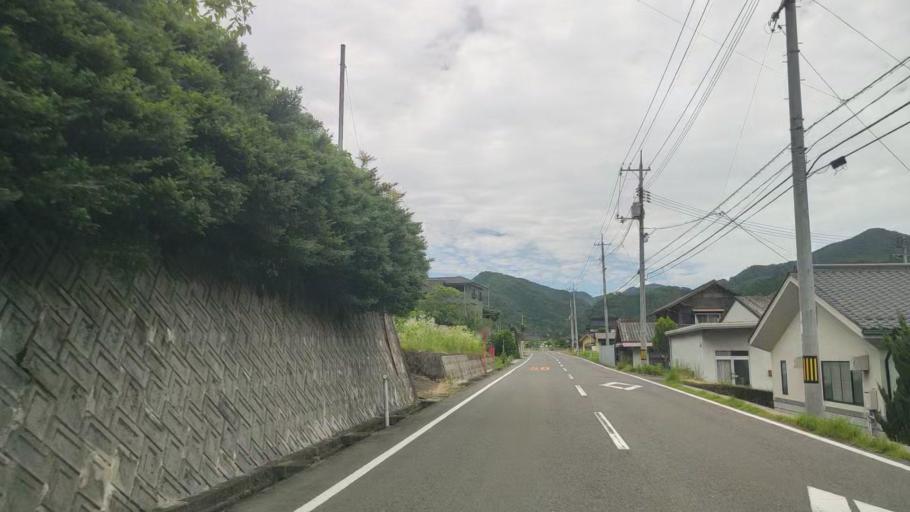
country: JP
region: Hyogo
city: Yamazakicho-nakabirose
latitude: 35.0959
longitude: 134.2964
